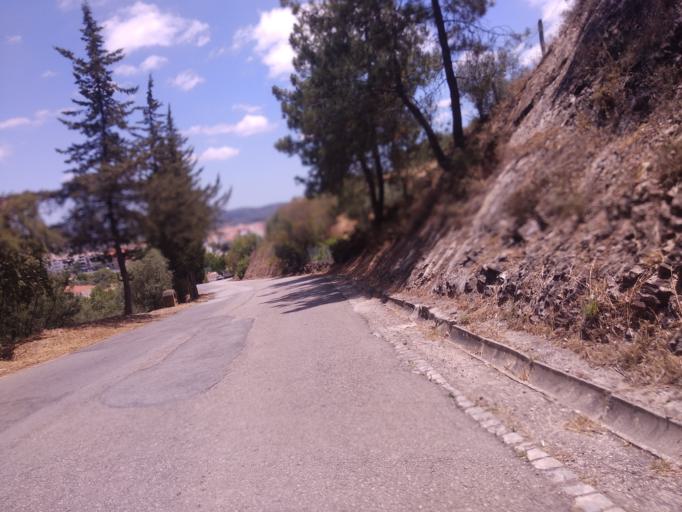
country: PT
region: Faro
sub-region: Sao Bras de Alportel
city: Sao Bras de Alportel
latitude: 37.1627
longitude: -7.8920
